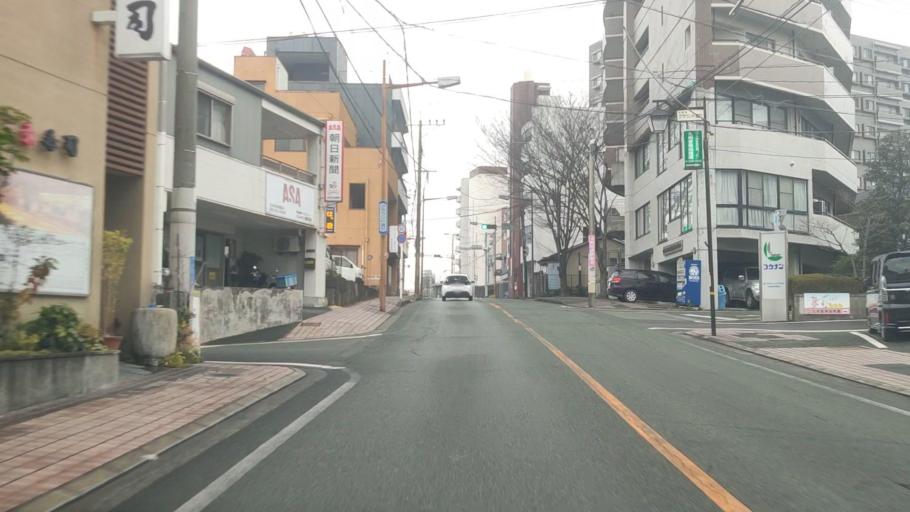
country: JP
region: Kumamoto
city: Kumamoto
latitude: 32.7926
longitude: 130.7375
